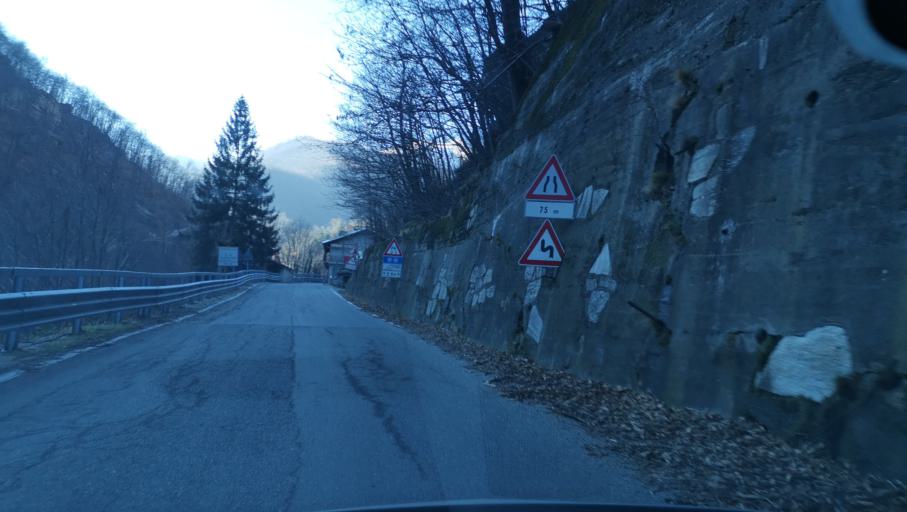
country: IT
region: Piedmont
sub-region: Provincia di Torino
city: Rora
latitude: 44.7940
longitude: 7.2162
